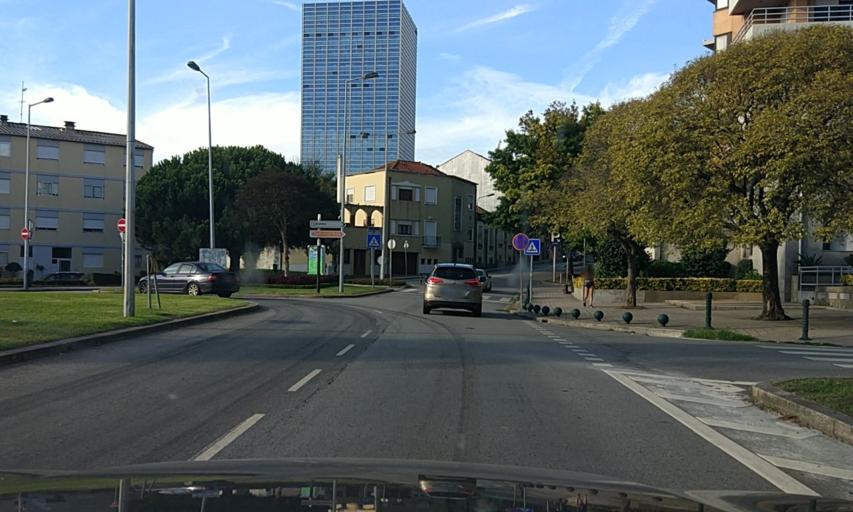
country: PT
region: Porto
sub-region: Matosinhos
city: Senhora da Hora
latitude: 41.1563
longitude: -8.6441
